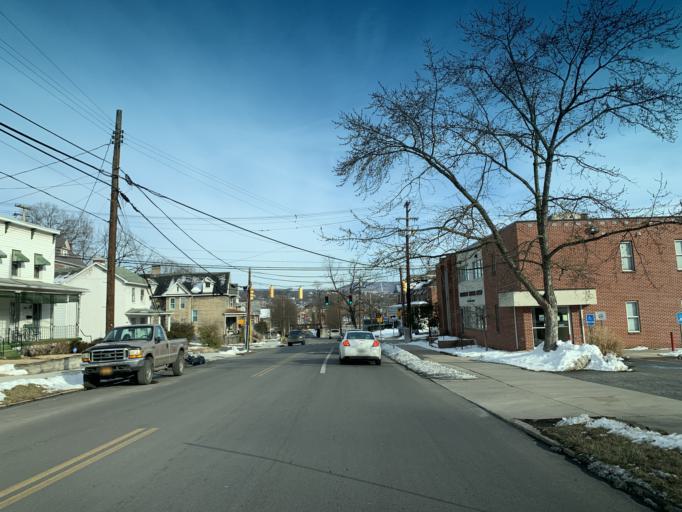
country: US
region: Maryland
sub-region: Allegany County
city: Cumberland
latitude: 39.6507
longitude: -78.7743
